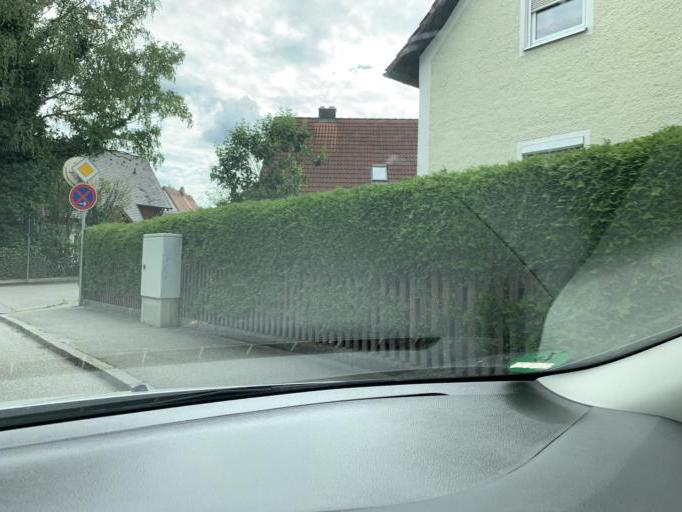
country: DE
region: Bavaria
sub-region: Upper Bavaria
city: Moosburg
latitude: 48.4722
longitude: 11.9410
